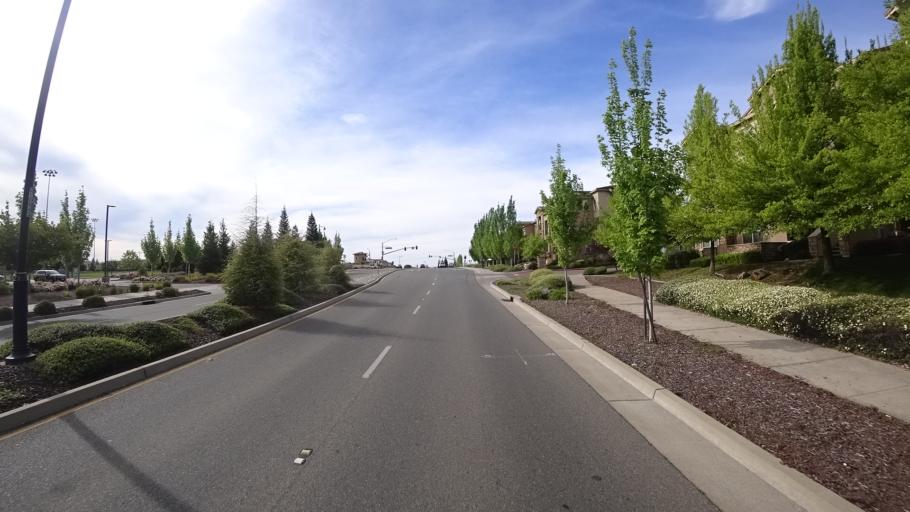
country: US
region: California
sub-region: Placer County
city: Lincoln
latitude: 38.8319
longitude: -121.2887
